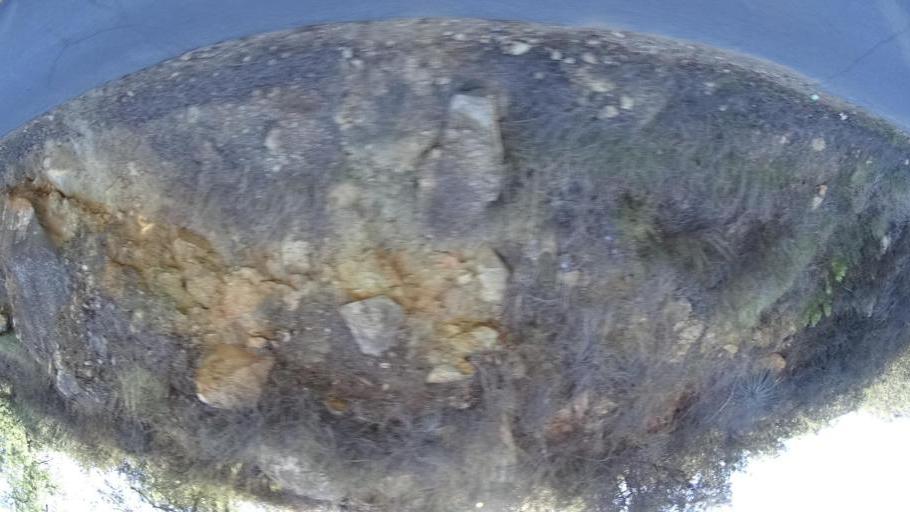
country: US
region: California
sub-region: San Diego County
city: Jamul
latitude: 32.7317
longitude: -116.8349
